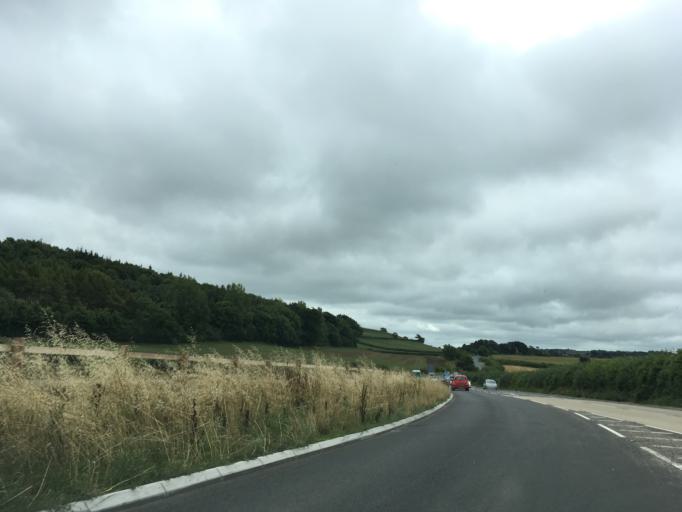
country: GB
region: England
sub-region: Bath and North East Somerset
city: Saltford
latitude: 51.3740
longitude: -2.4777
